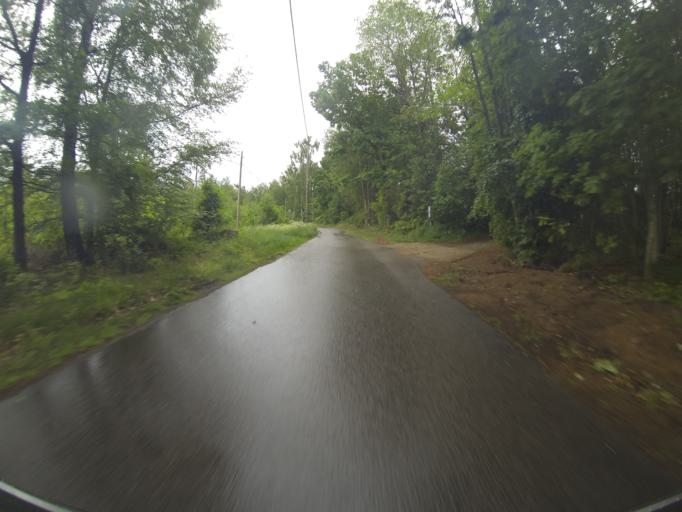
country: SE
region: Blekinge
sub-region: Ronneby Kommun
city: Ronneby
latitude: 56.1710
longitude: 15.3112
